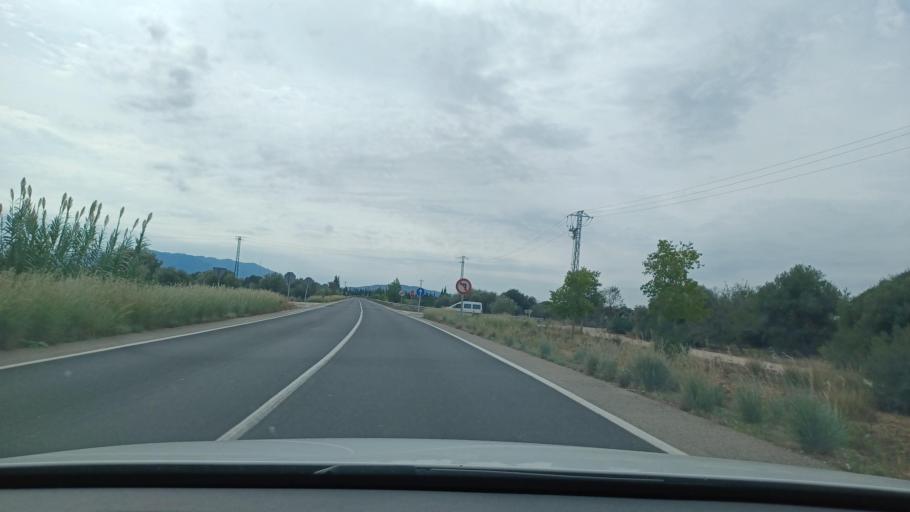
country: ES
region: Catalonia
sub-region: Provincia de Tarragona
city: Santa Barbara
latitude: 40.7607
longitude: 0.5020
